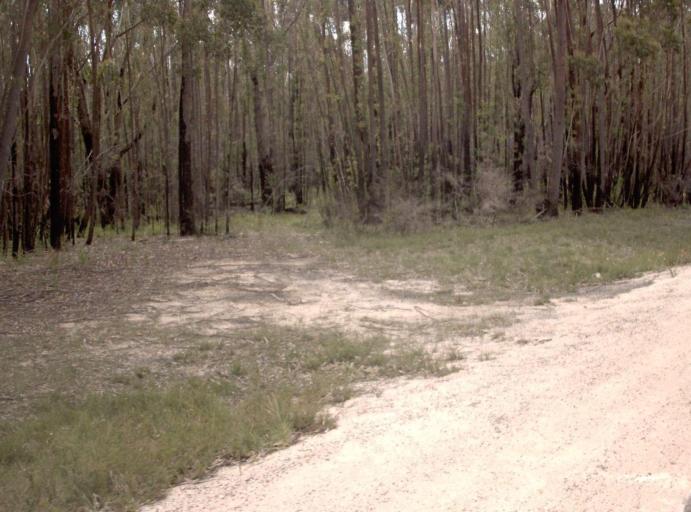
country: AU
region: New South Wales
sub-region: Bega Valley
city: Eden
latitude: -37.5296
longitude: 149.4874
